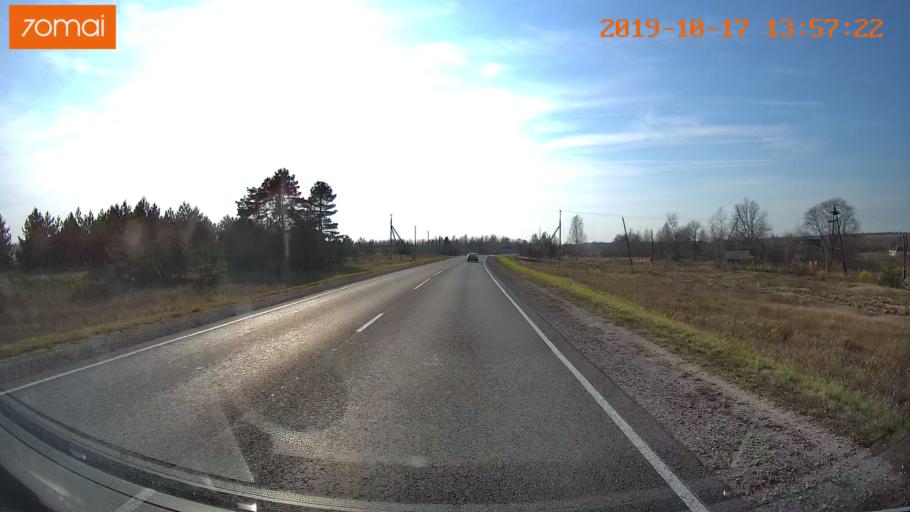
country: RU
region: Rjazan
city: Spas-Klepiki
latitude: 55.1441
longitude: 40.2482
